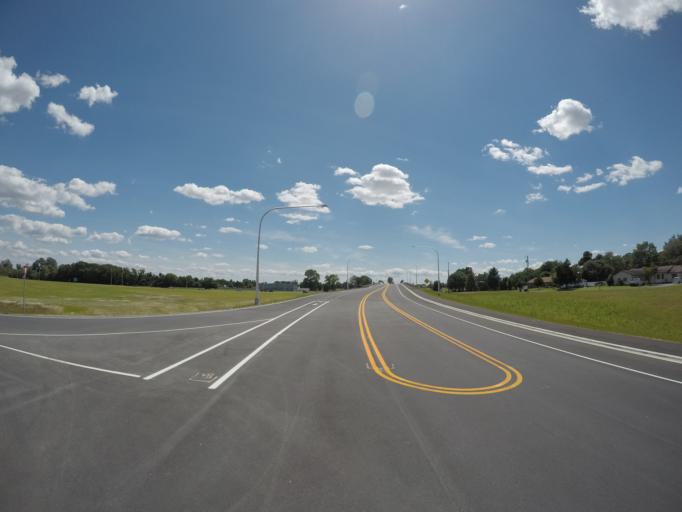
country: US
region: Delaware
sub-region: Sussex County
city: Milford
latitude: 38.9273
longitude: -75.4107
